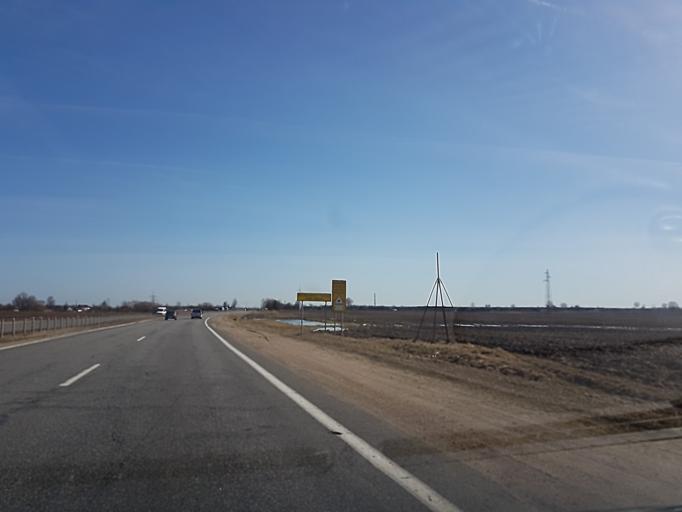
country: BY
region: Minsk
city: Dukora
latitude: 53.6750
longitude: 27.9311
